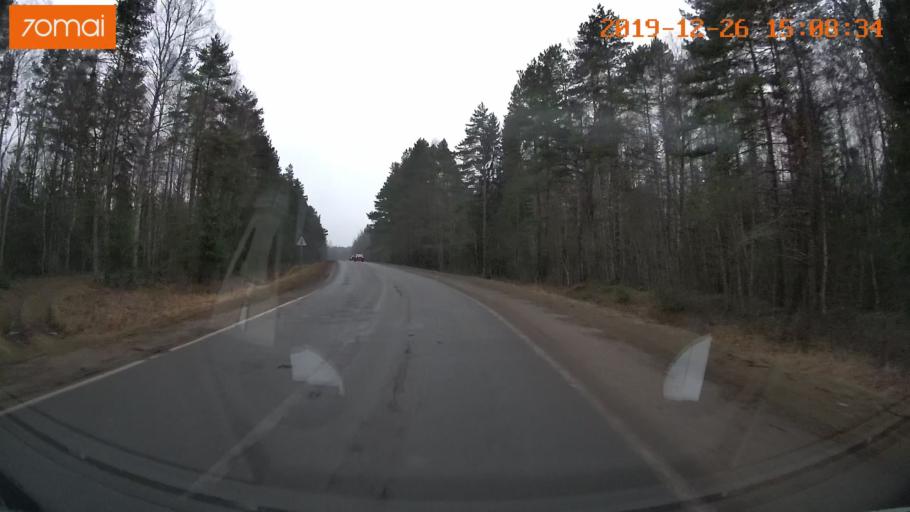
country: RU
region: Jaroslavl
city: Rybinsk
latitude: 58.1584
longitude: 38.8371
